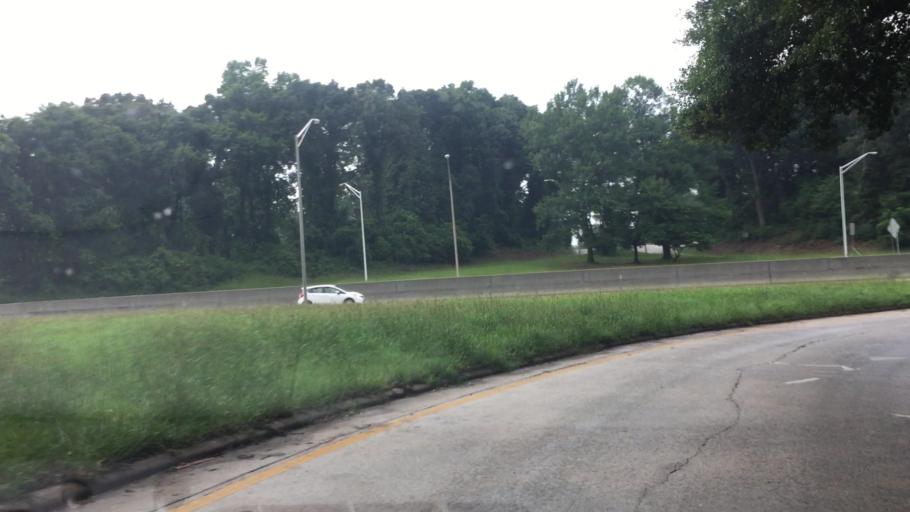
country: US
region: Georgia
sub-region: Fulton County
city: East Point
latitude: 33.6976
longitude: -84.4309
